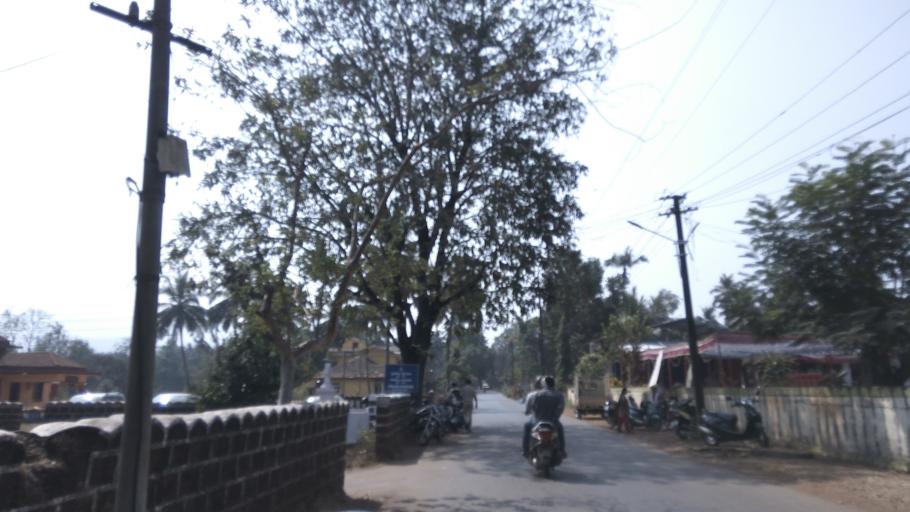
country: IN
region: Goa
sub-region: South Goa
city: Sanguem
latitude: 15.3409
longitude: 74.2427
